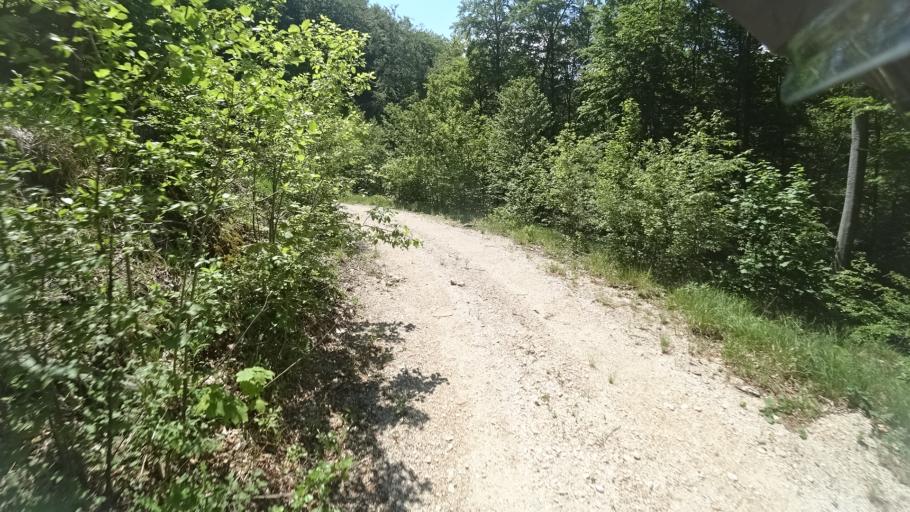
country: BA
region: Federation of Bosnia and Herzegovina
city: Orasac
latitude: 44.5669
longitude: 15.8532
